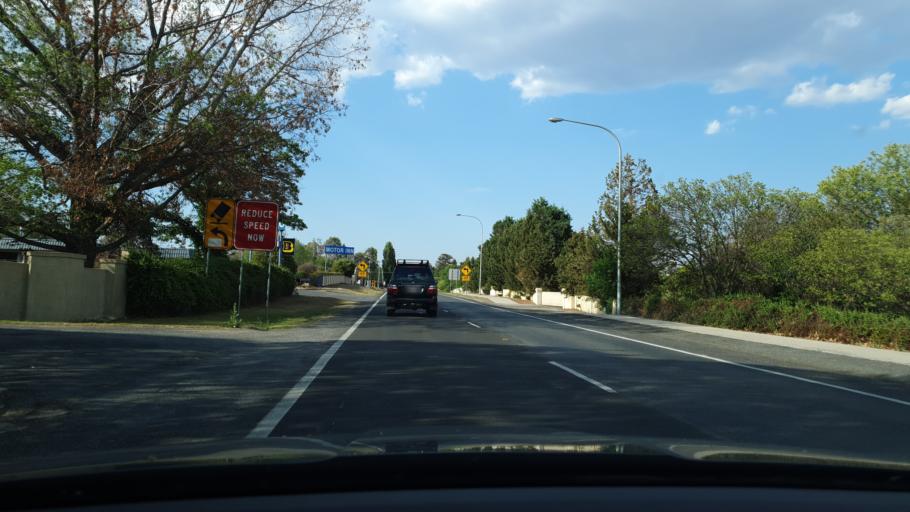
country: AU
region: New South Wales
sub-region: Tenterfield Municipality
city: Carrolls Creek
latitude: -29.0430
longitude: 152.0211
